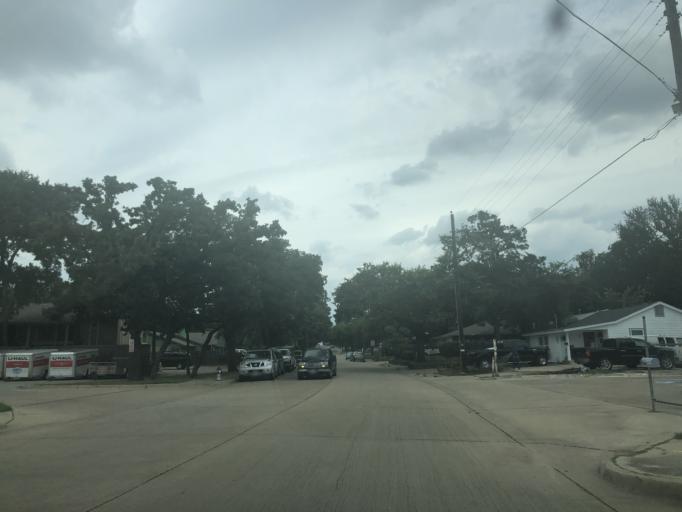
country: US
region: Texas
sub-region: Dallas County
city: Irving
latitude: 32.8011
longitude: -96.9299
